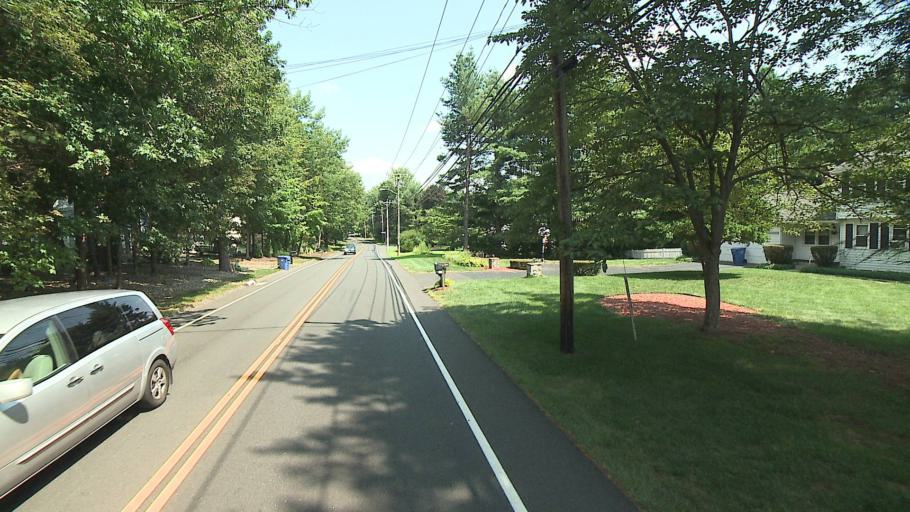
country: US
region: Connecticut
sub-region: Hartford County
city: Collinsville
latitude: 41.7761
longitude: -72.8904
